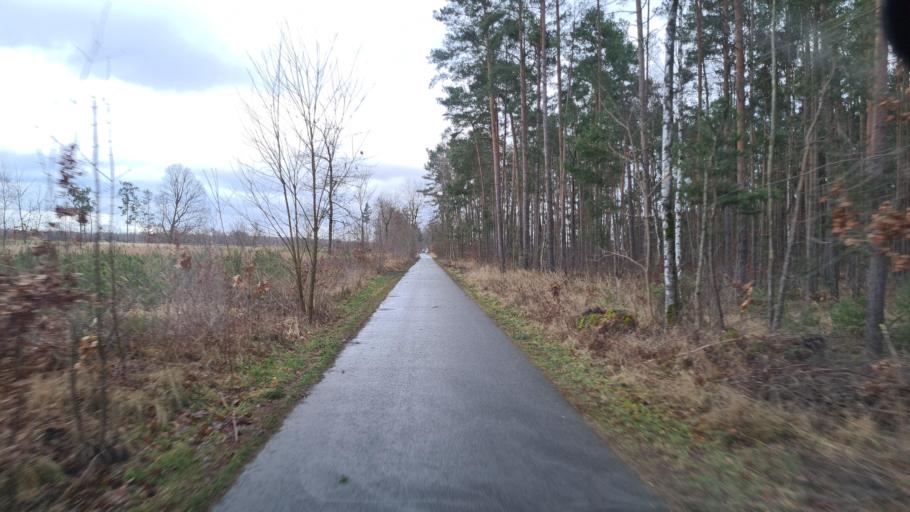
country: DE
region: Brandenburg
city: Kroppen
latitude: 51.4011
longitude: 13.7859
